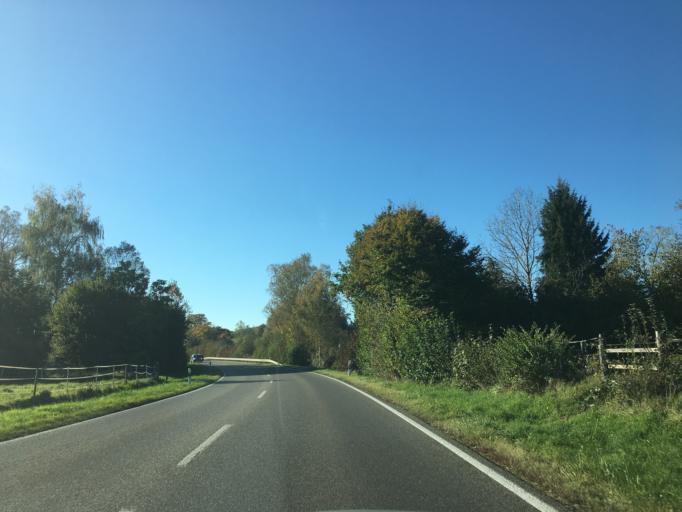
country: CH
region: Thurgau
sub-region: Kreuzlingen District
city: Gottlieben
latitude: 47.7000
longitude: 9.1556
